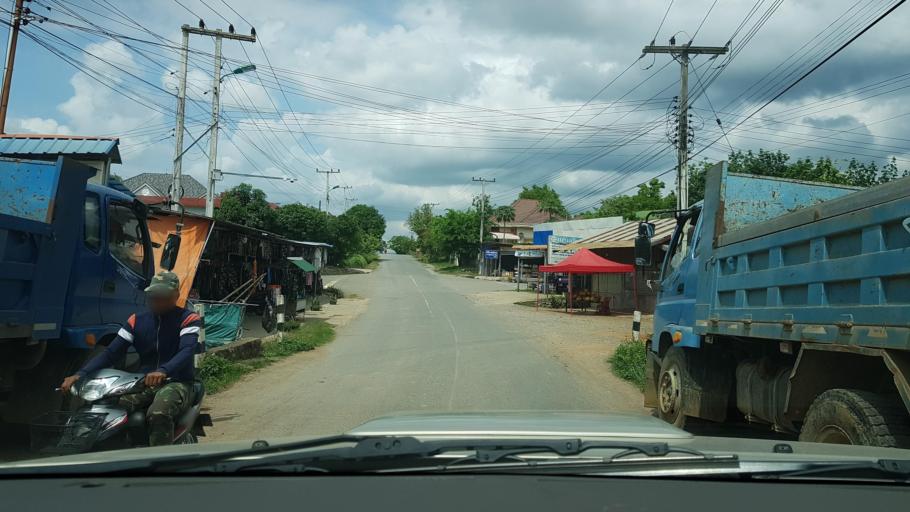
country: LA
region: Loungnamtha
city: Muang Nale
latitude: 20.1475
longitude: 101.4688
